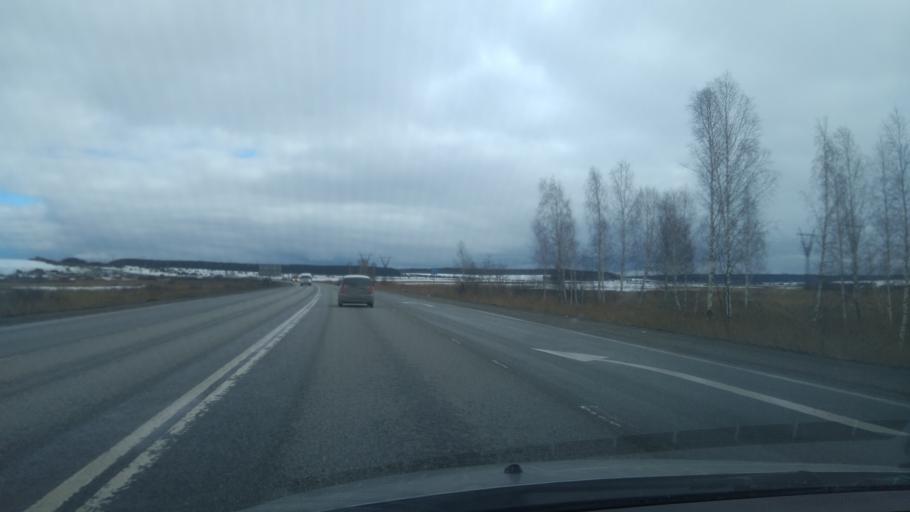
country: RU
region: Sverdlovsk
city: Achit
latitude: 56.7862
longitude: 57.8884
